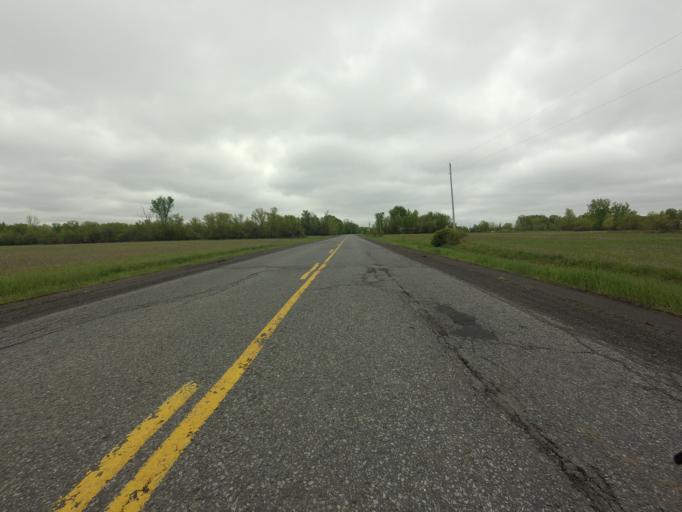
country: US
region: New York
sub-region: St. Lawrence County
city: Norfolk
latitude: 44.9847
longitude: -75.1569
